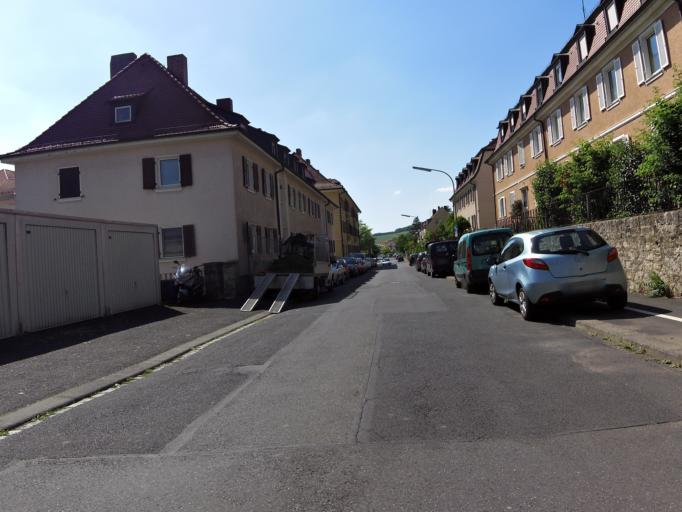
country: DE
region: Bavaria
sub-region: Regierungsbezirk Unterfranken
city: Wuerzburg
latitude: 49.8035
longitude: 9.9531
